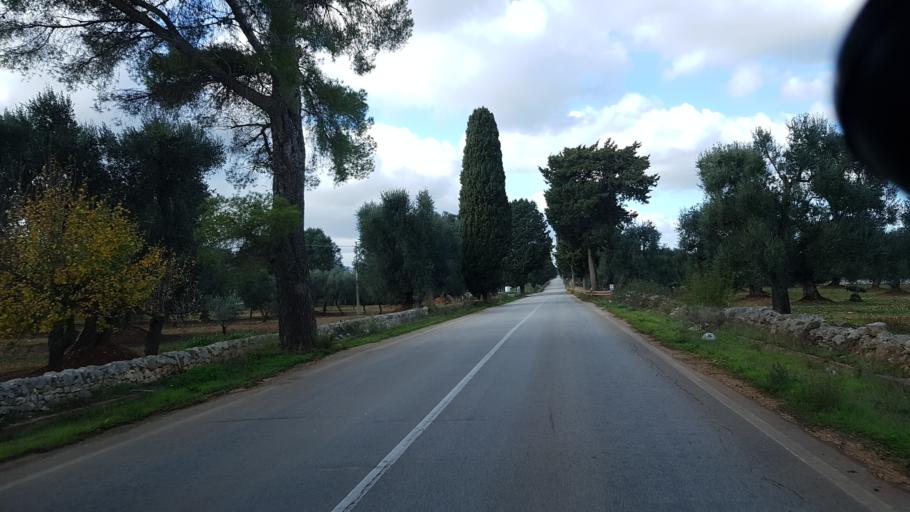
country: IT
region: Apulia
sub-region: Provincia di Brindisi
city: Montalbano
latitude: 40.7624
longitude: 17.5249
